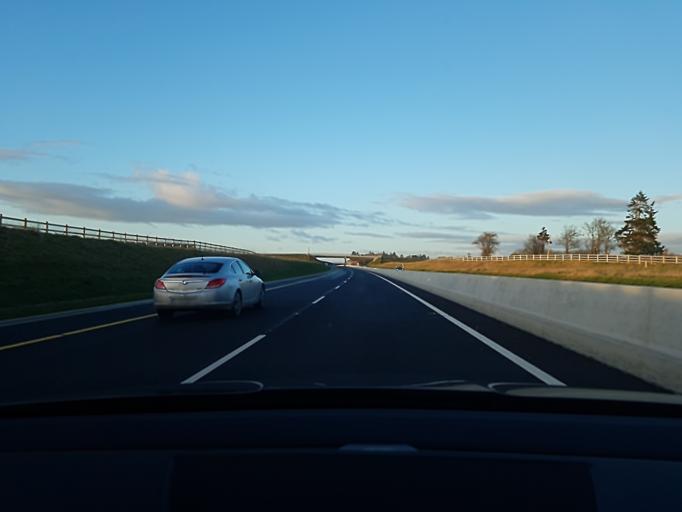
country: IE
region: Connaught
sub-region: County Galway
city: Athenry
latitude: 53.3351
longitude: -8.8024
